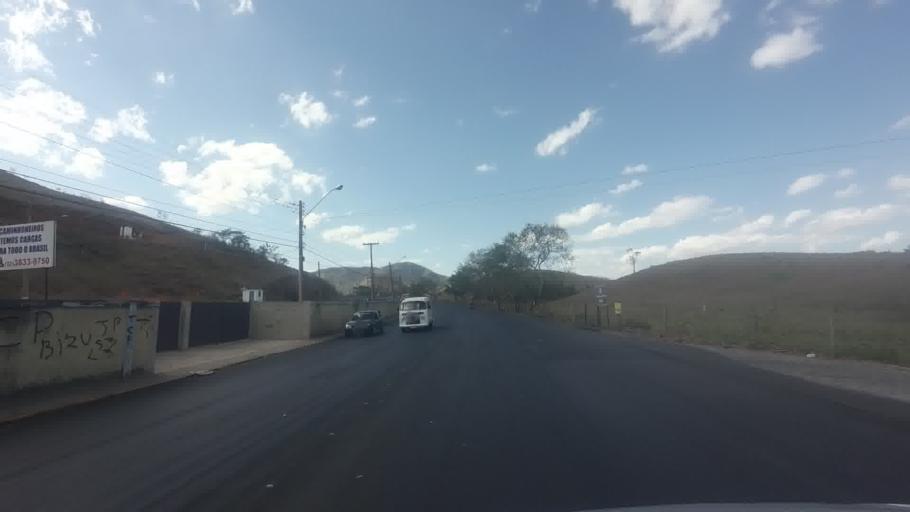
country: BR
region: Rio de Janeiro
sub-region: Bom Jesus Do Itabapoana
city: Bom Jesus do Itabapoana
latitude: -21.1412
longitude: -41.6631
